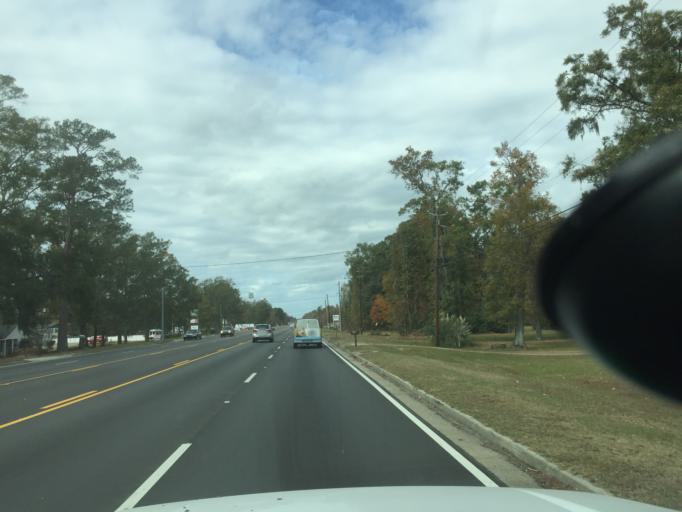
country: US
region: Georgia
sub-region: Chatham County
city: Garden City
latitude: 32.0893
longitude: -81.1810
